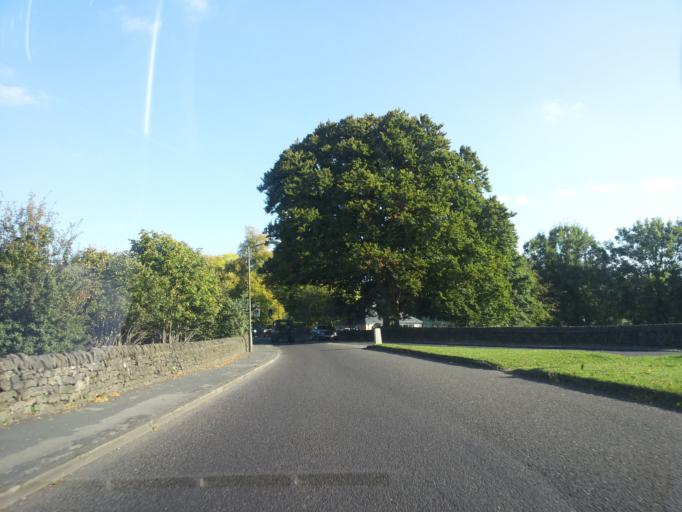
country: GB
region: England
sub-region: Derbyshire
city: Bakewell
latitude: 53.2469
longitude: -1.6219
